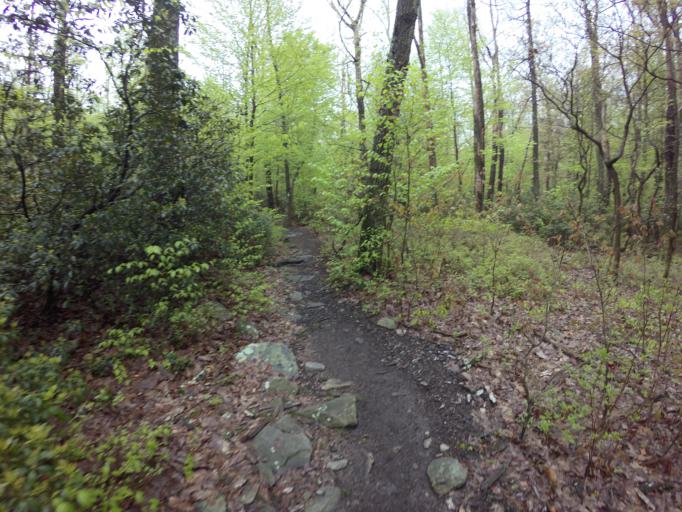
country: US
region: Maryland
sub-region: Washington County
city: Boonsboro
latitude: 39.5235
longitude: -77.6155
